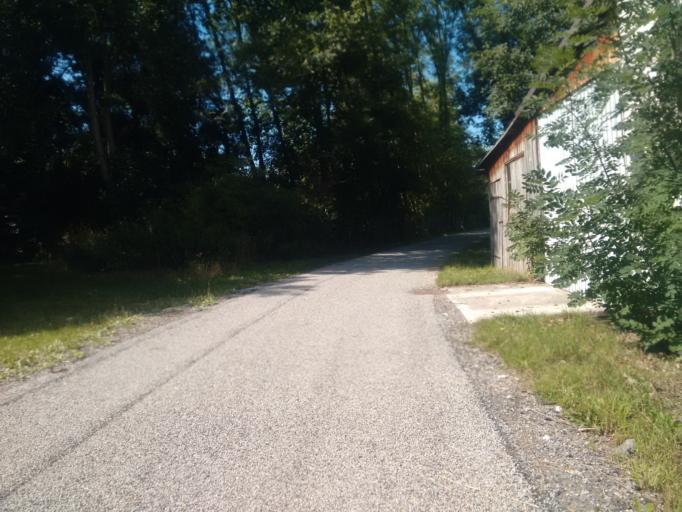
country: AT
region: Upper Austria
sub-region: Wels-Land
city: Steinhaus
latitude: 48.1396
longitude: 14.0026
